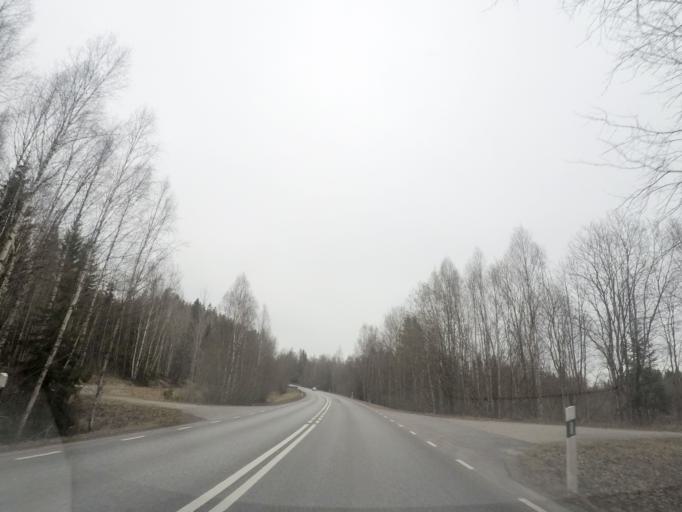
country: SE
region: Vaestmanland
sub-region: Skinnskattebergs Kommun
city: Skinnskatteberg
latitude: 59.8411
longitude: 15.6830
